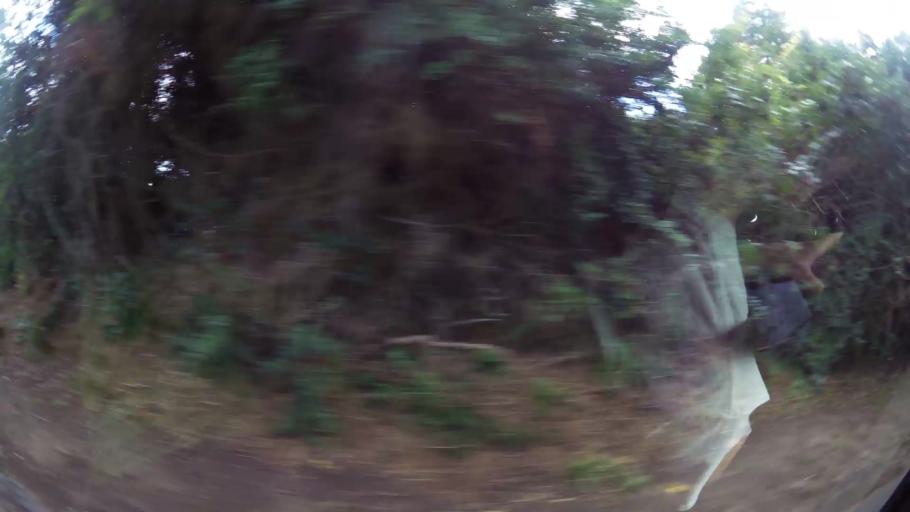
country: ZA
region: Western Cape
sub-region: Eden District Municipality
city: Knysna
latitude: -34.0549
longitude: 23.0778
